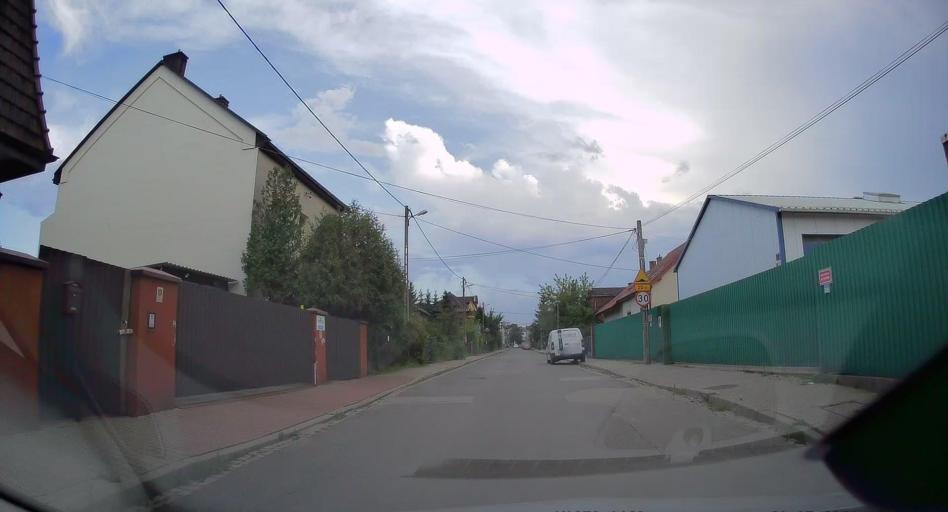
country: PL
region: Lesser Poland Voivodeship
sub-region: Krakow
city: Krakow
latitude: 50.0264
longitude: 19.9965
